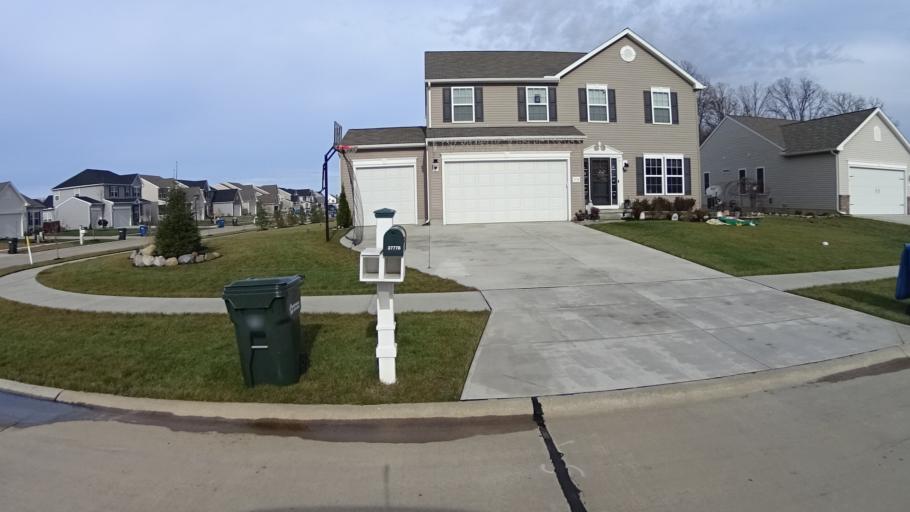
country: US
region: Ohio
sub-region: Lorain County
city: North Ridgeville
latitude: 41.3595
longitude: -82.0460
